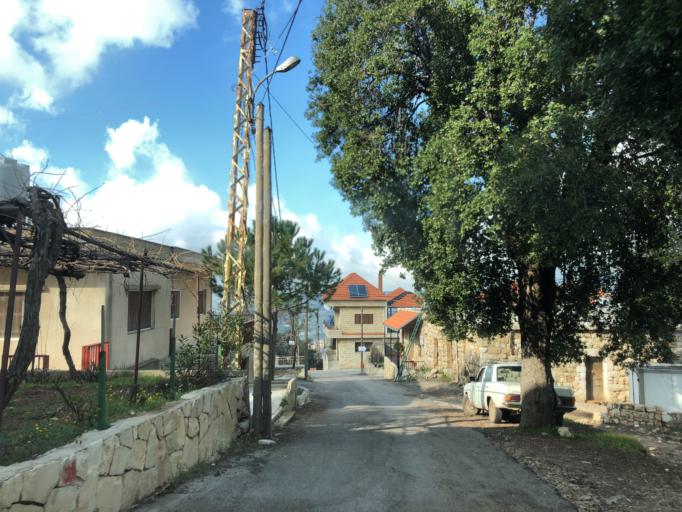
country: LB
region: Liban-Nord
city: Amioun
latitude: 34.2062
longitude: 35.8414
